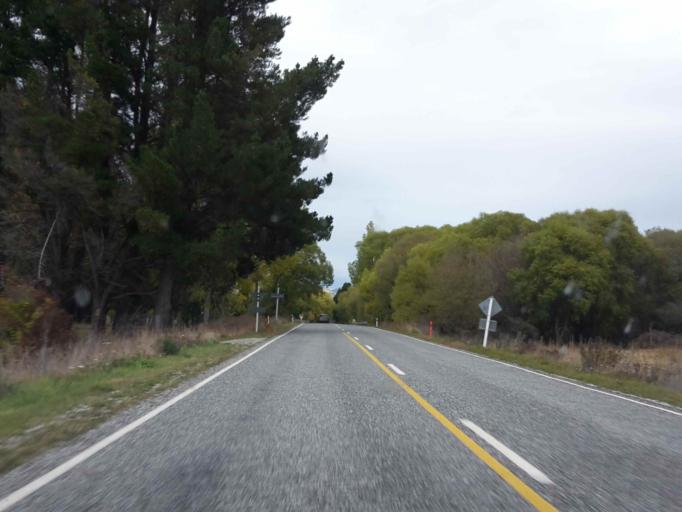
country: NZ
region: Otago
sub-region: Queenstown-Lakes District
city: Wanaka
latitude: -44.8311
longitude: 169.0595
